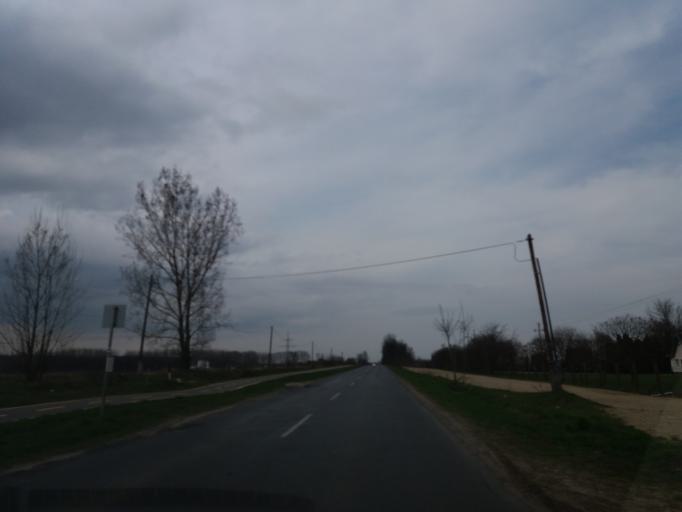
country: HU
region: Szabolcs-Szatmar-Bereg
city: Anarcs
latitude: 48.1913
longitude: 22.0992
